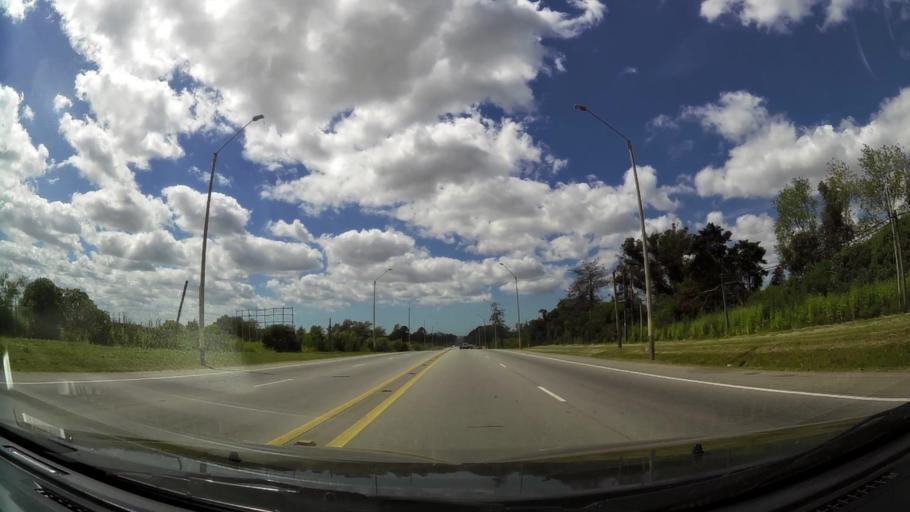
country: UY
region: Canelones
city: Colonia Nicolich
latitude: -34.8011
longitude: -56.0570
